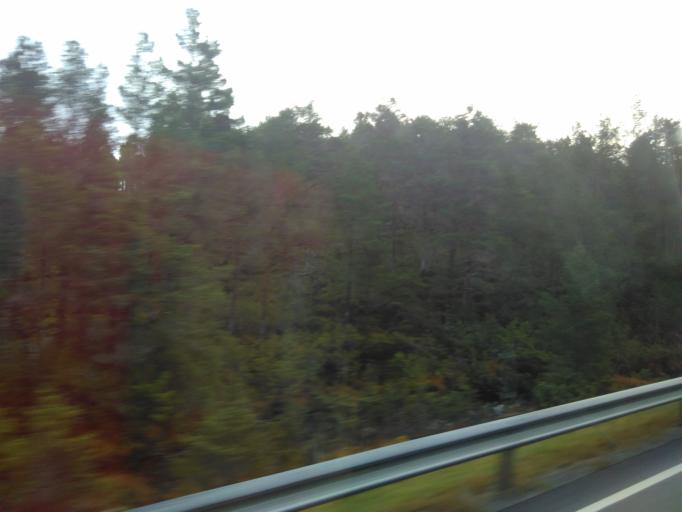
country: NO
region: Sor-Trondelag
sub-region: Hitra
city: Fillan
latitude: 63.5711
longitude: 9.0321
